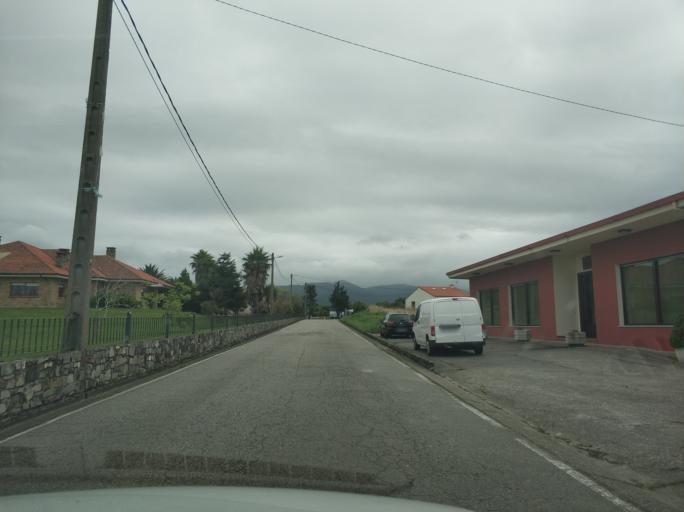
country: ES
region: Asturias
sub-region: Province of Asturias
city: Cudillero
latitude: 43.5717
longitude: -6.2369
